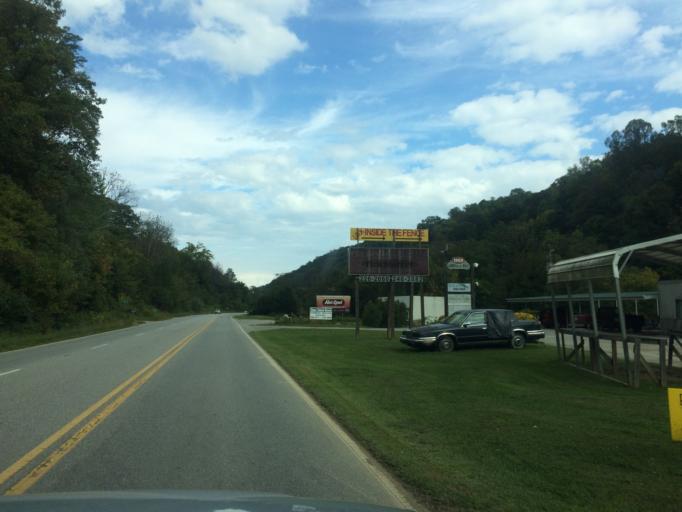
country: US
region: North Carolina
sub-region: Haywood County
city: Canton
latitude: 35.5364
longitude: -82.8017
